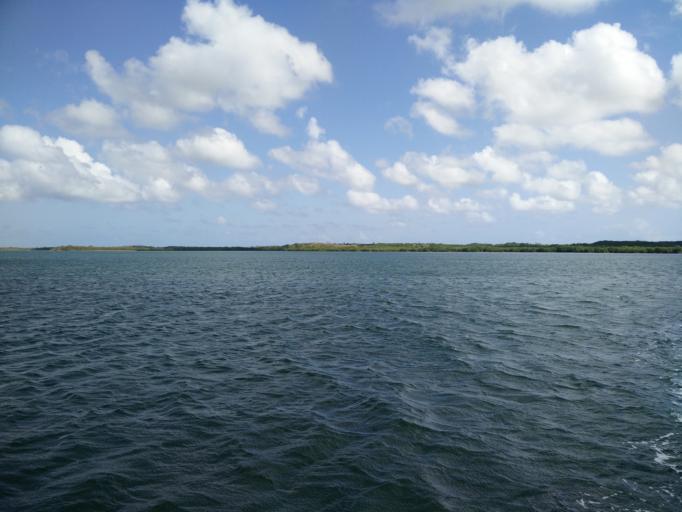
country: GP
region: Guadeloupe
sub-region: Guadeloupe
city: Petit-Canal
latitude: 16.3766
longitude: -61.4988
